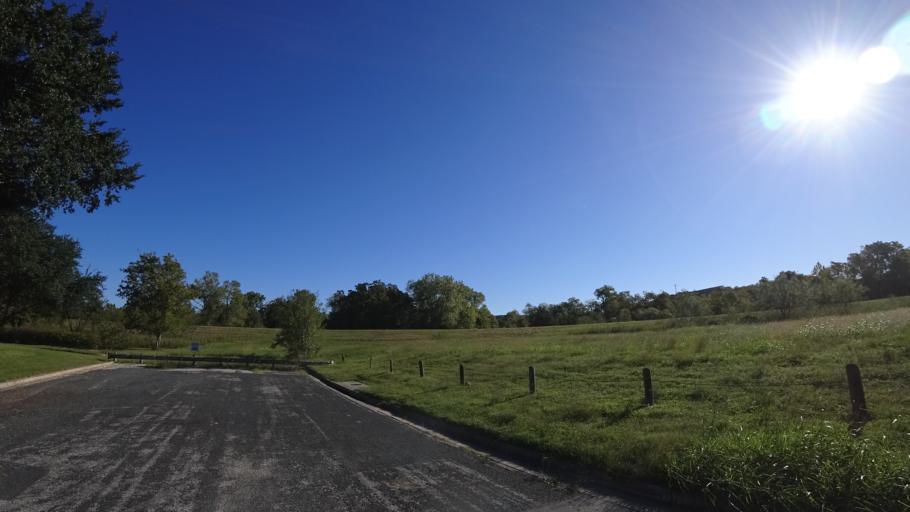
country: US
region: Texas
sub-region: Travis County
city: Hornsby Bend
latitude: 30.3120
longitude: -97.6504
